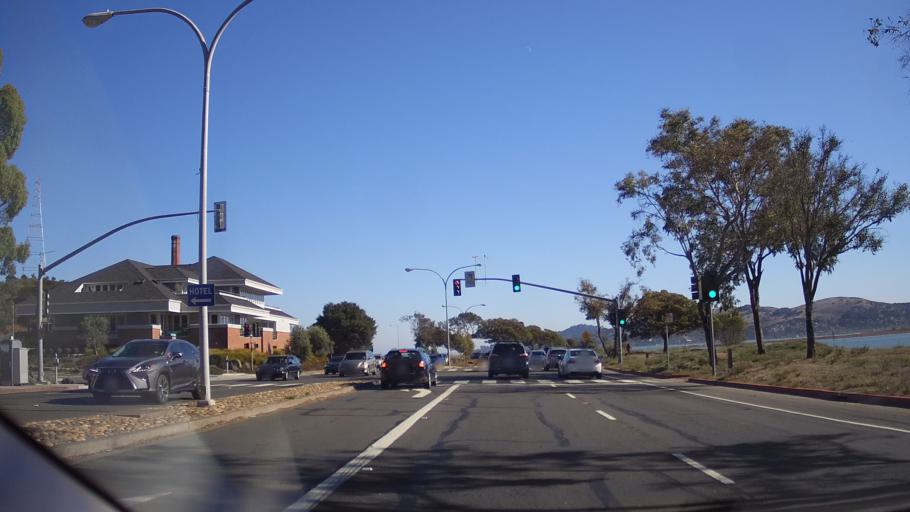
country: US
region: California
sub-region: Marin County
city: Corte Madera
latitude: 37.9458
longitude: -122.5080
